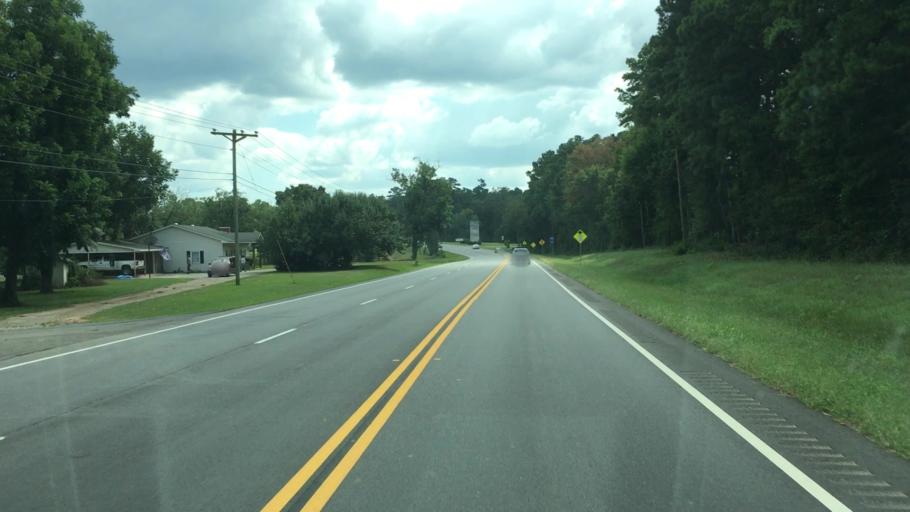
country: US
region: Georgia
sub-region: Putnam County
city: Jefferson
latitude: 33.4208
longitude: -83.3714
